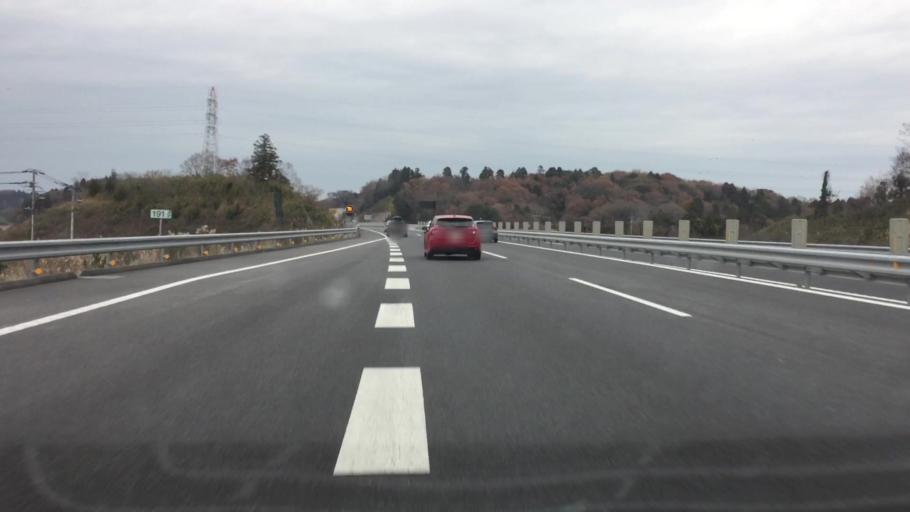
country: JP
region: Chiba
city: Sawara
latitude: 35.8653
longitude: 140.3914
